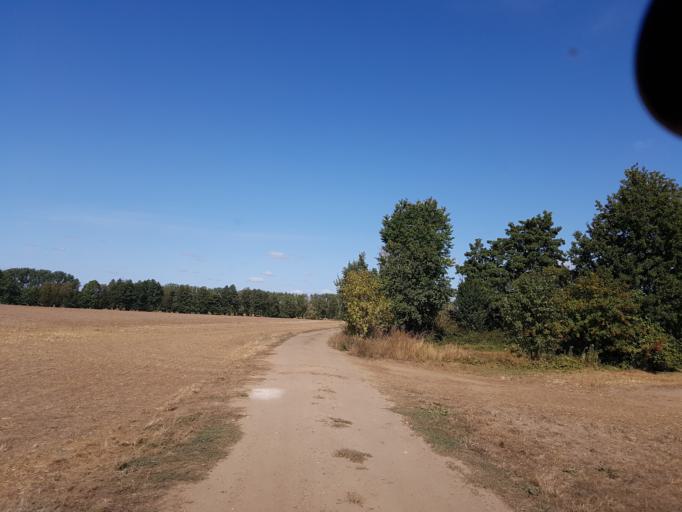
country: DE
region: Brandenburg
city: Luckau
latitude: 51.8434
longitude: 13.6360
